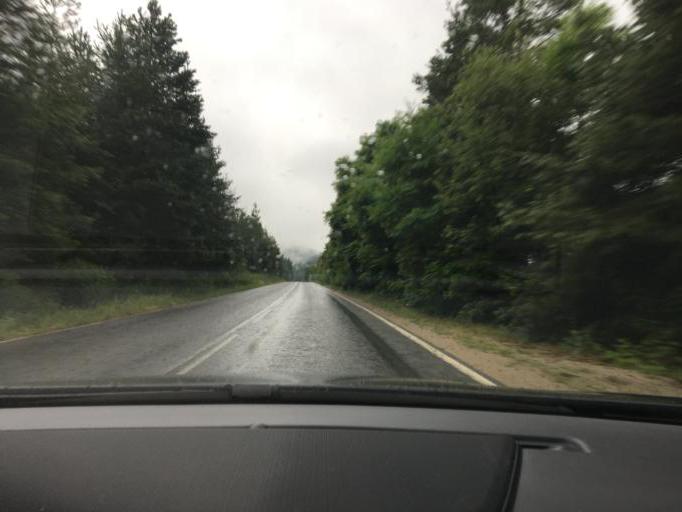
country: MK
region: Kriva Palanka
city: Kriva Palanka
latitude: 42.2289
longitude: 22.4846
